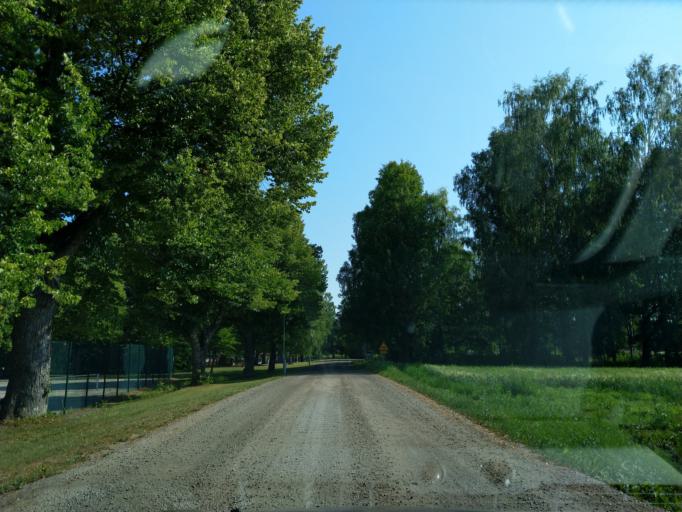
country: FI
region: Satakunta
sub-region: Pori
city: Noormarkku
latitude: 61.5916
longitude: 21.8822
